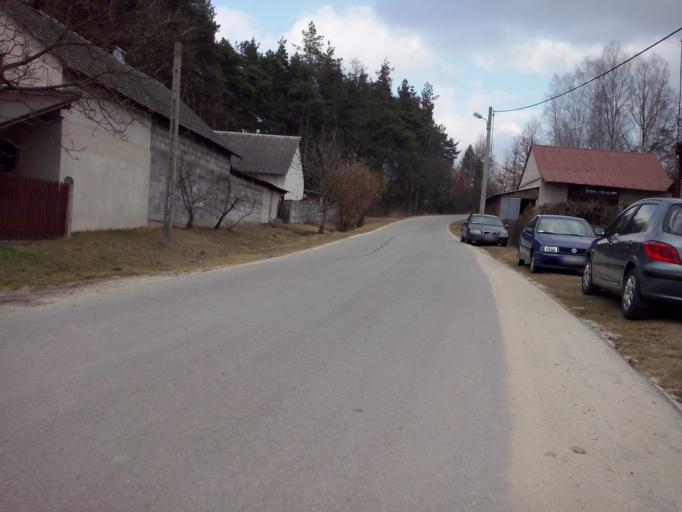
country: PL
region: Subcarpathian Voivodeship
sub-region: Powiat nizanski
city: Krzeszow
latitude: 50.4263
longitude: 22.3369
